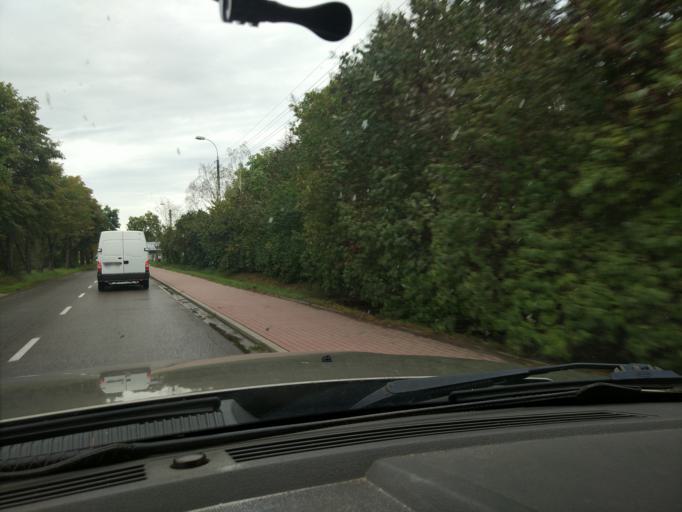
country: PL
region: Masovian Voivodeship
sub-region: Powiat pruszkowski
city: Brwinow
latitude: 52.1515
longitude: 20.7276
